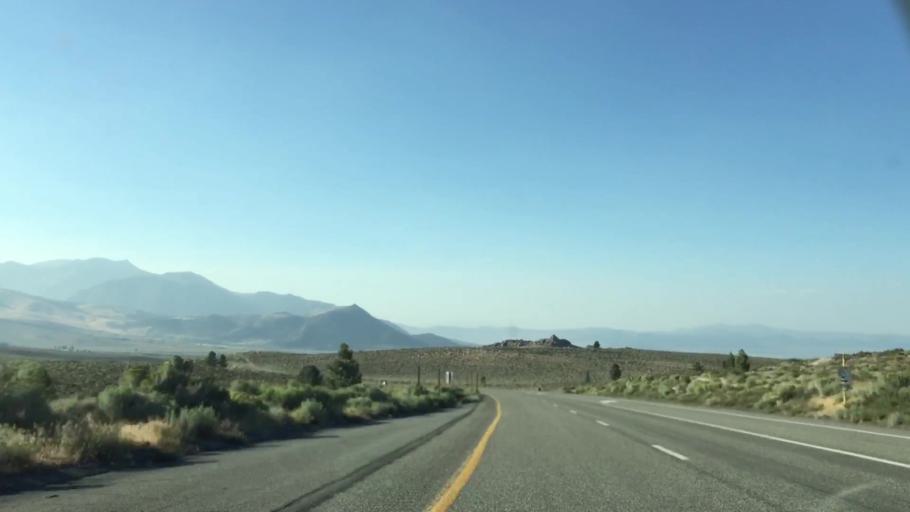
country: US
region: California
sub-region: Mono County
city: Mammoth Lakes
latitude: 37.8387
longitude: -119.0703
